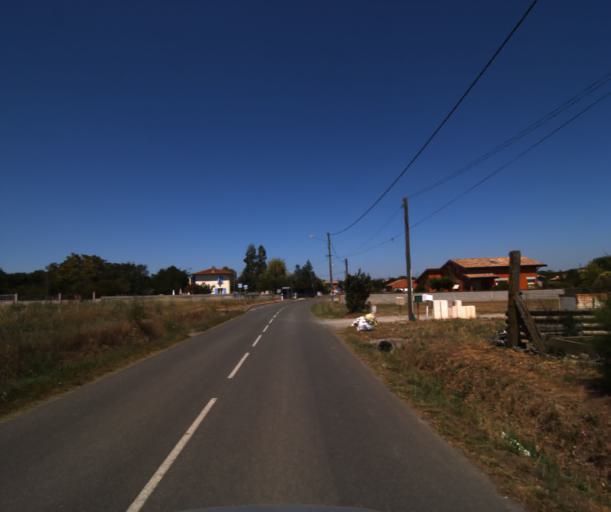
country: FR
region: Midi-Pyrenees
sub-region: Departement de la Haute-Garonne
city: Seysses
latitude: 43.4484
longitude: 1.2968
